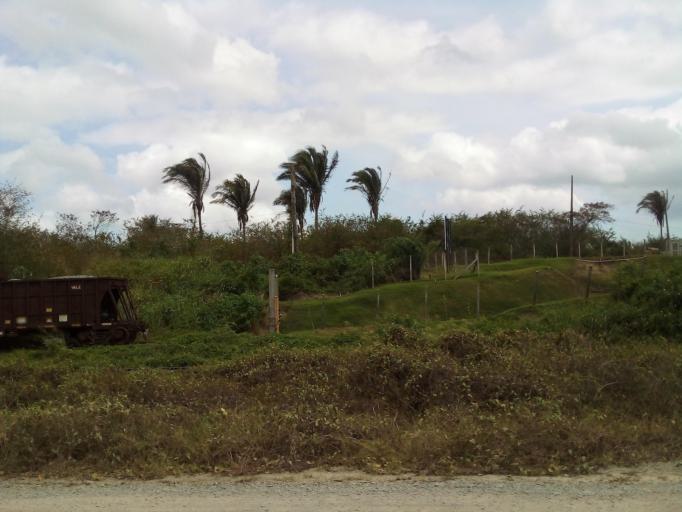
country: BR
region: Maranhao
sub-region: Icatu
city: Icatu
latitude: -2.9270
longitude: -44.3450
